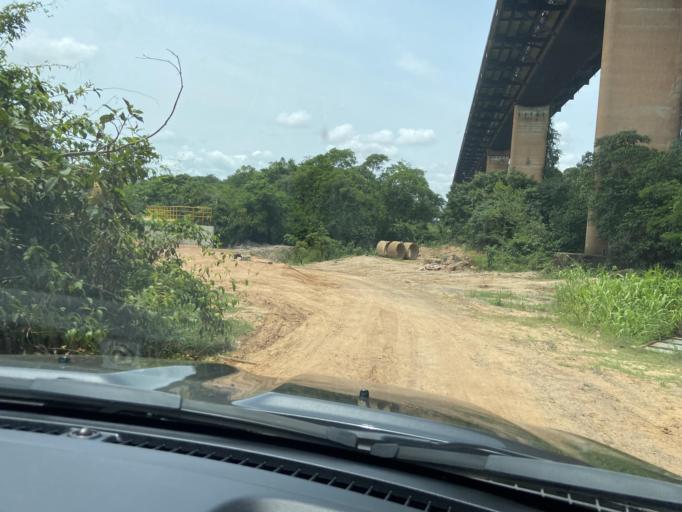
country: BR
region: Para
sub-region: Maraba
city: Maraba
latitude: -5.3079
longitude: -49.0741
